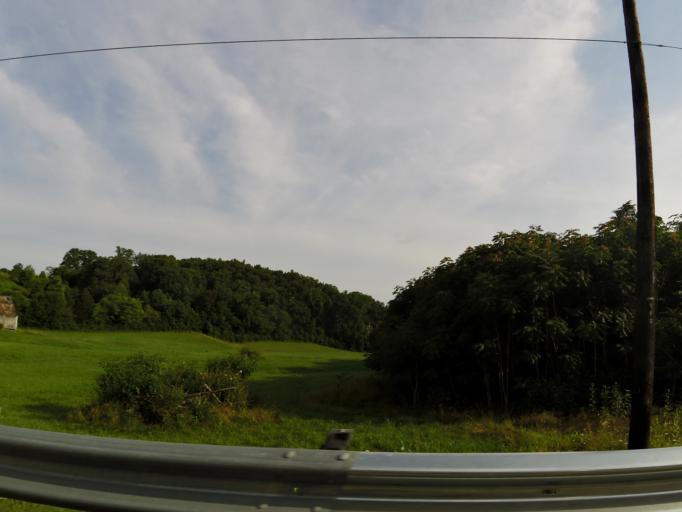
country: US
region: Tennessee
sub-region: Humphreys County
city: McEwen
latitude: 36.0970
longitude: -87.5848
